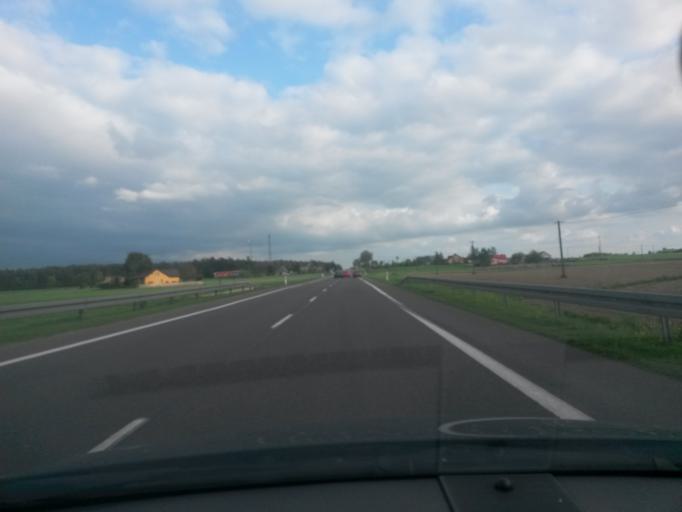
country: PL
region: Masovian Voivodeship
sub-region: Powiat plocki
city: Starozreby
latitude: 52.6592
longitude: 20.0799
